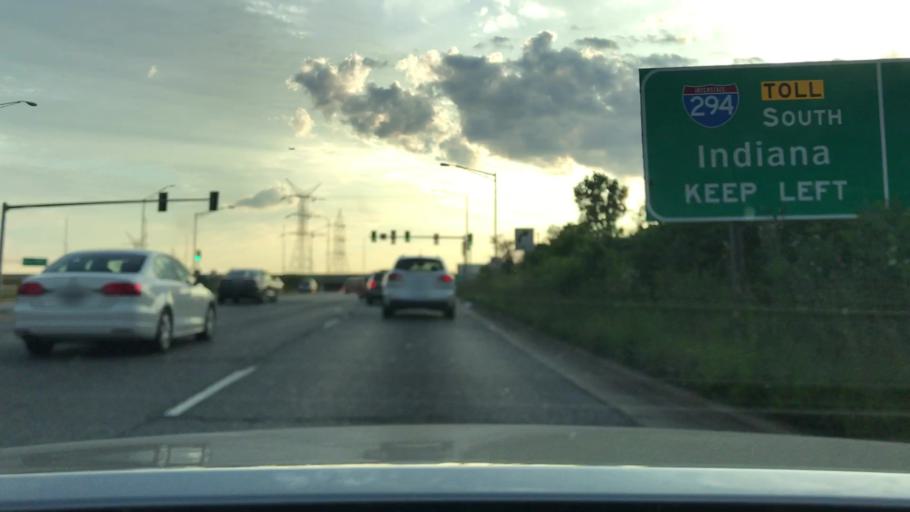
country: US
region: Illinois
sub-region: Cook County
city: Hickory Hills
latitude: 41.7189
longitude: -87.8040
